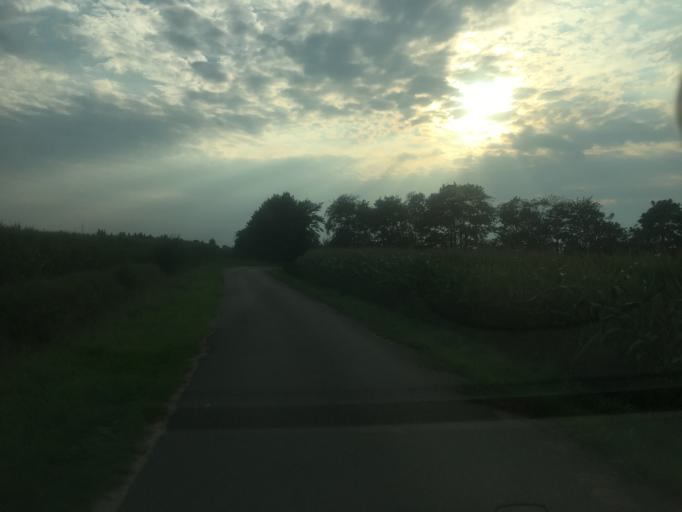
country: DK
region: South Denmark
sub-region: Tonder Kommune
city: Logumkloster
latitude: 55.0418
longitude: 8.9143
